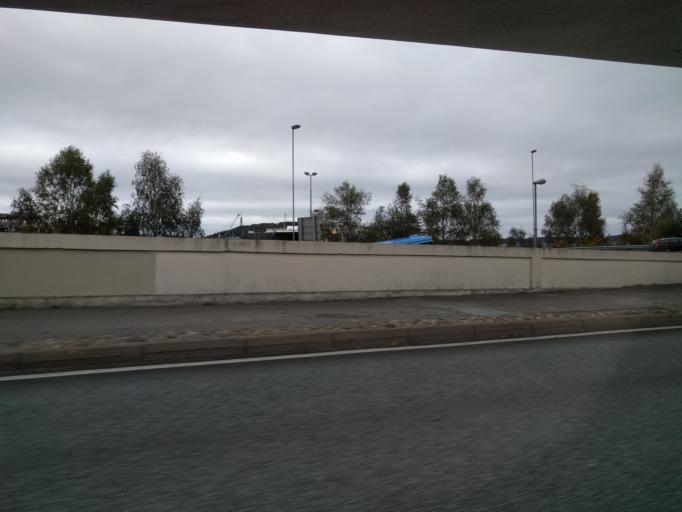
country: NO
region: Vest-Agder
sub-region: Kristiansand
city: Kristiansand
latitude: 58.1455
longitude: 7.9826
